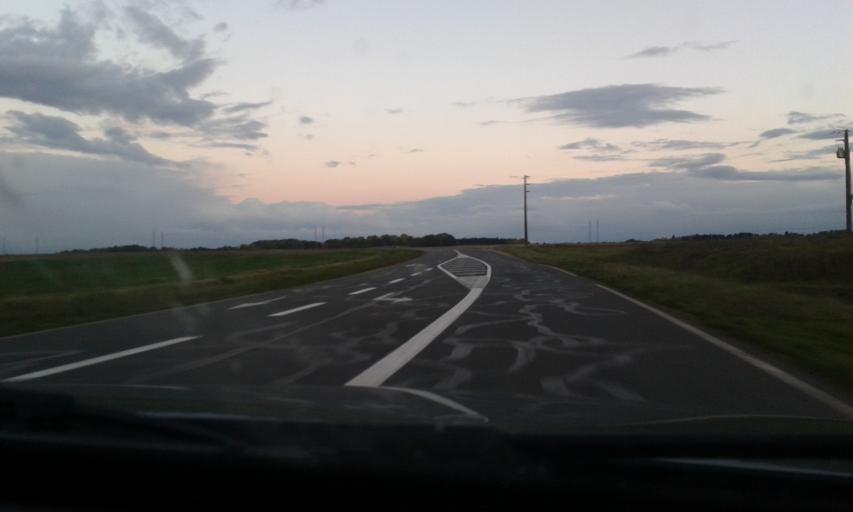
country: FR
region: Centre
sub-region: Departement du Loiret
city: Meung-sur-Loire
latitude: 47.8569
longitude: 1.7060
